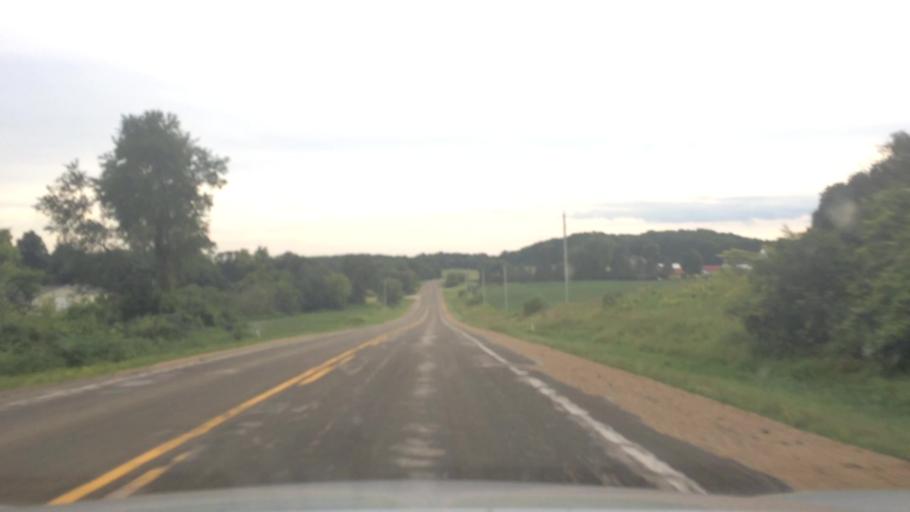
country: US
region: Wisconsin
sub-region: Columbia County
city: Lodi
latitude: 43.3279
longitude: -89.4865
